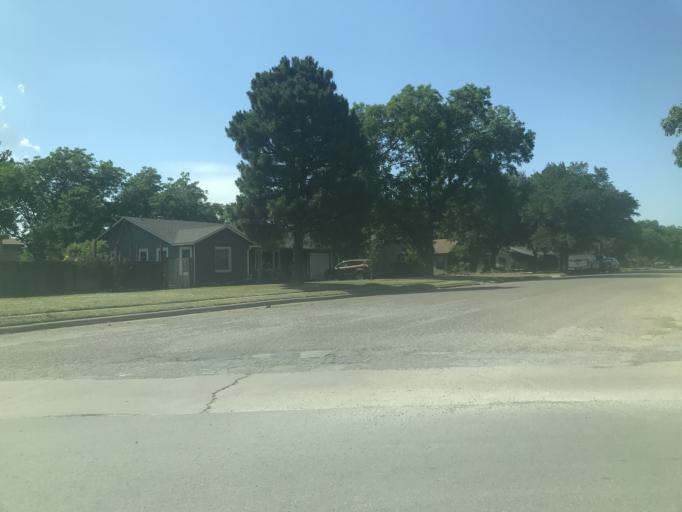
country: US
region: Texas
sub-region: Taylor County
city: Abilene
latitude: 32.4343
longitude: -99.7513
